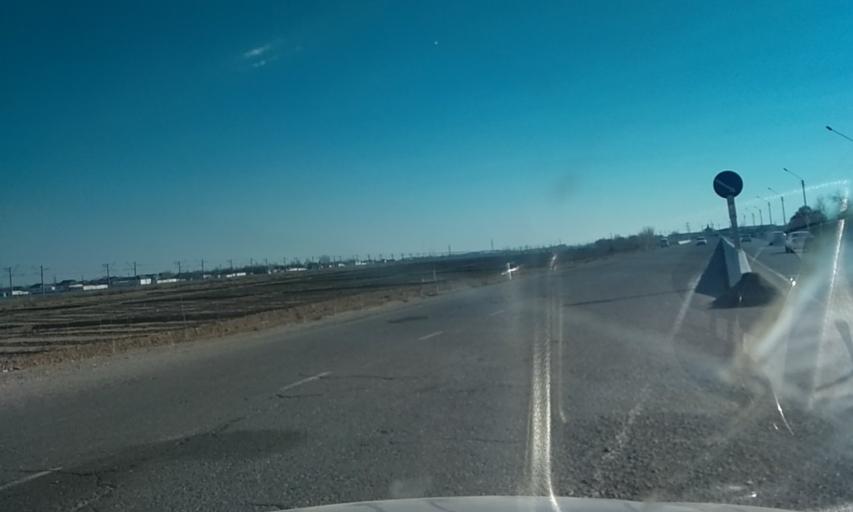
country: UZ
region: Sirdaryo
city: Guliston
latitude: 40.4653
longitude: 68.7720
